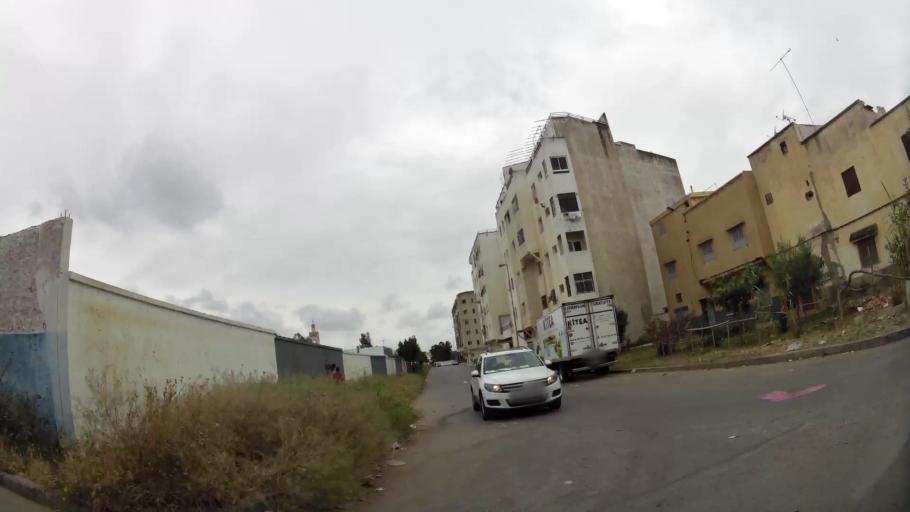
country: MA
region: Rabat-Sale-Zemmour-Zaer
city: Sale
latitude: 34.0409
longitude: -6.8075
